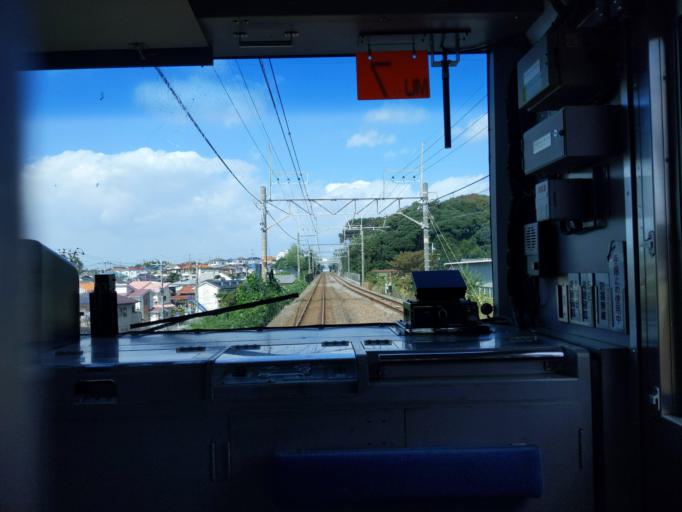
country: JP
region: Chiba
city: Funabashi
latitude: 35.7356
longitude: 139.9638
